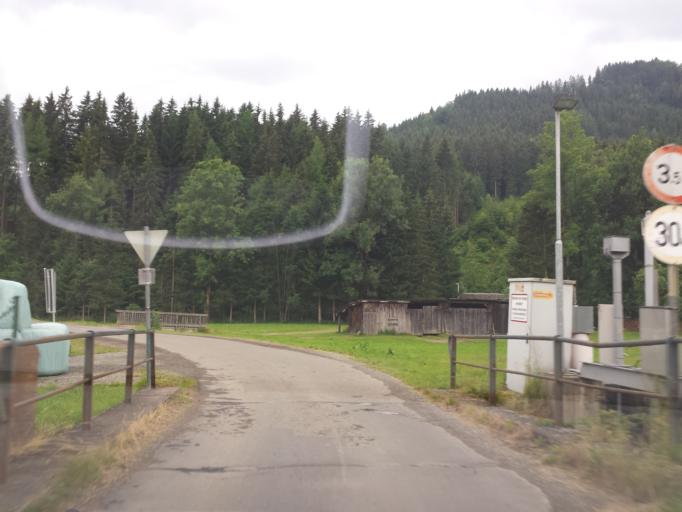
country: AT
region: Styria
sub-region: Politischer Bezirk Murtal
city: Spielberg bei Knittelfeld
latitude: 47.2348
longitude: 14.7764
